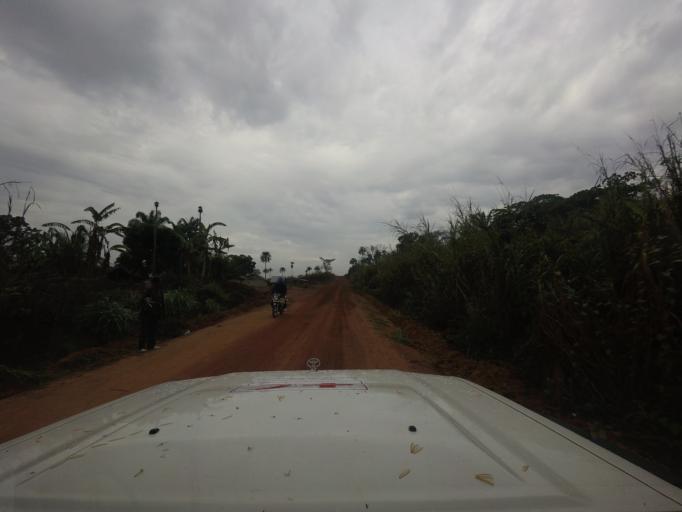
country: LR
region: Lofa
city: Voinjama
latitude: 8.3964
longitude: -9.7954
